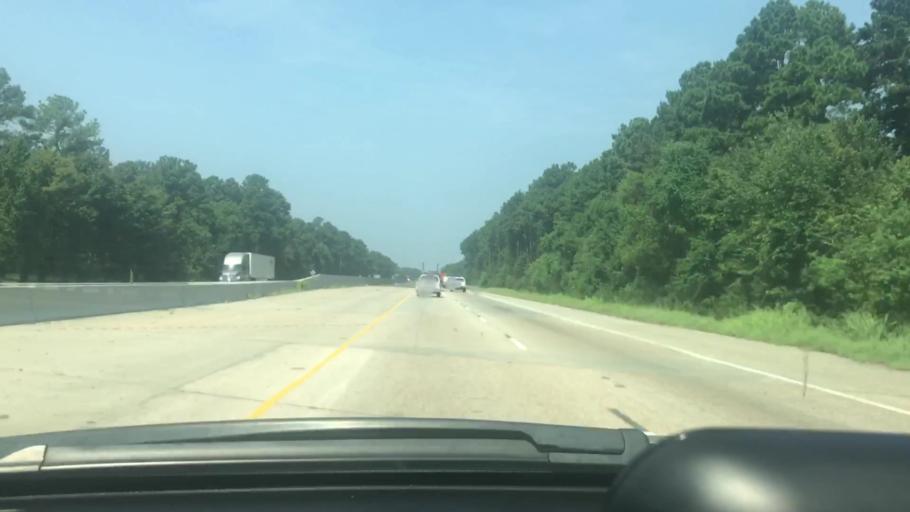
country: US
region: Louisiana
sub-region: Livingston Parish
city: Albany
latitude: 30.4747
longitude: -90.6536
